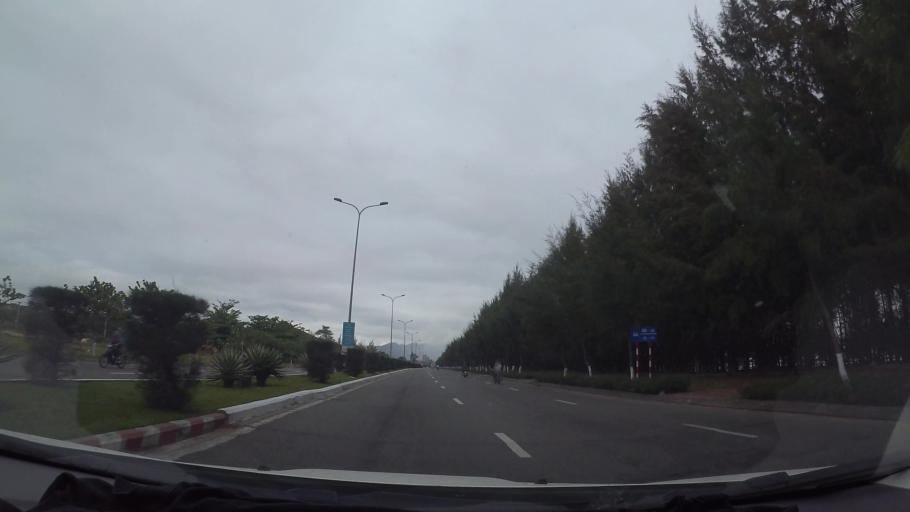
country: VN
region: Da Nang
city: Lien Chieu
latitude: 16.0938
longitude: 108.1476
